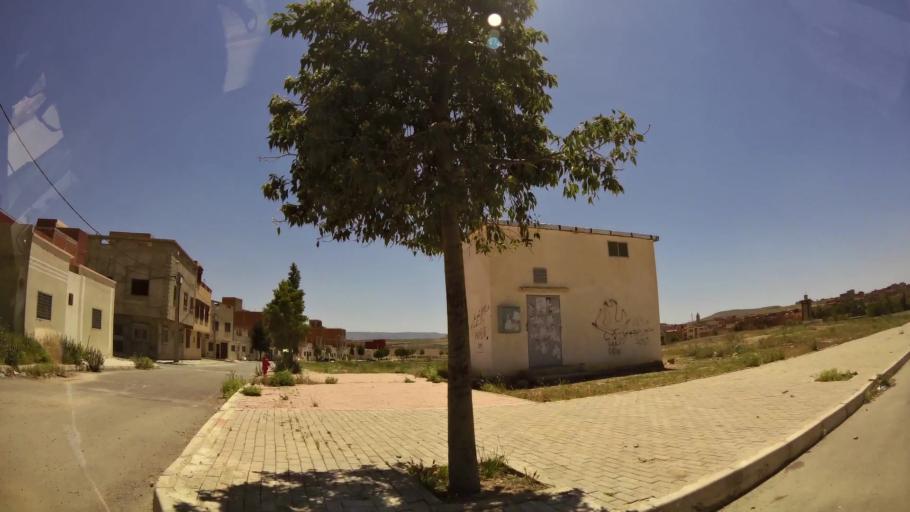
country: MA
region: Oriental
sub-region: Oujda-Angad
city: Oujda
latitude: 34.6560
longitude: -1.9308
